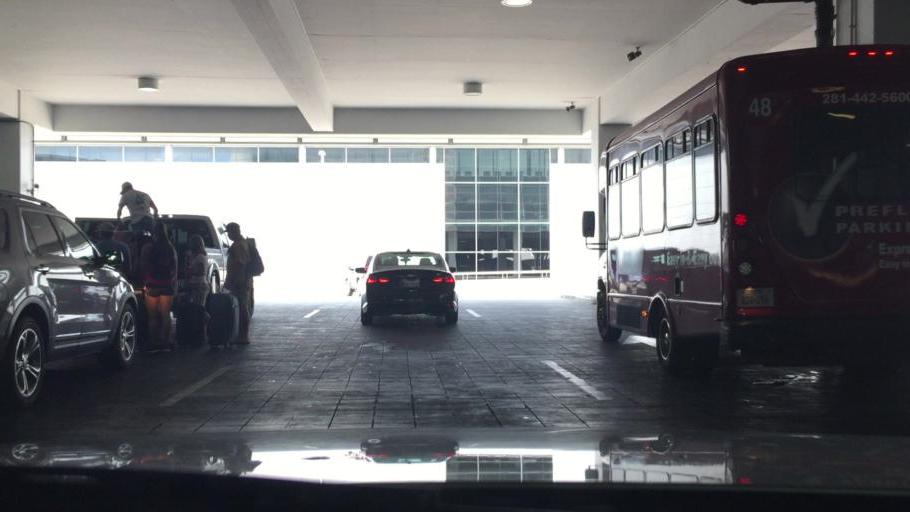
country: US
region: Texas
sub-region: Harris County
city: Aldine
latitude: 29.9866
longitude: -95.3343
